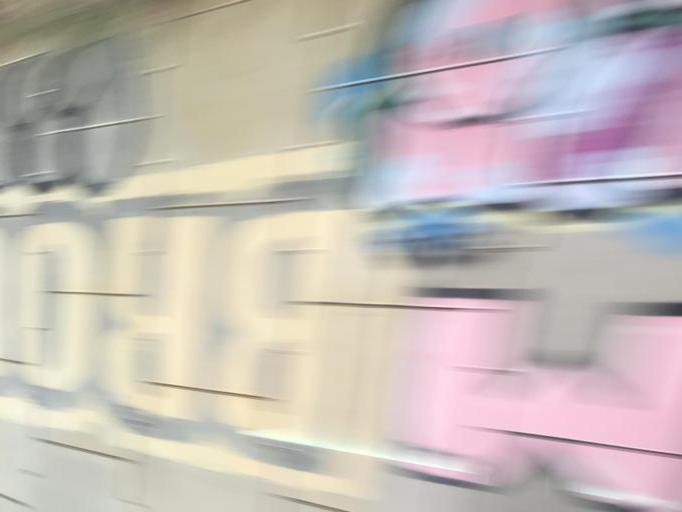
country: ES
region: Castille and Leon
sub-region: Provincia de Burgos
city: Pradanos de Bureba
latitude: 42.4962
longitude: -3.3562
